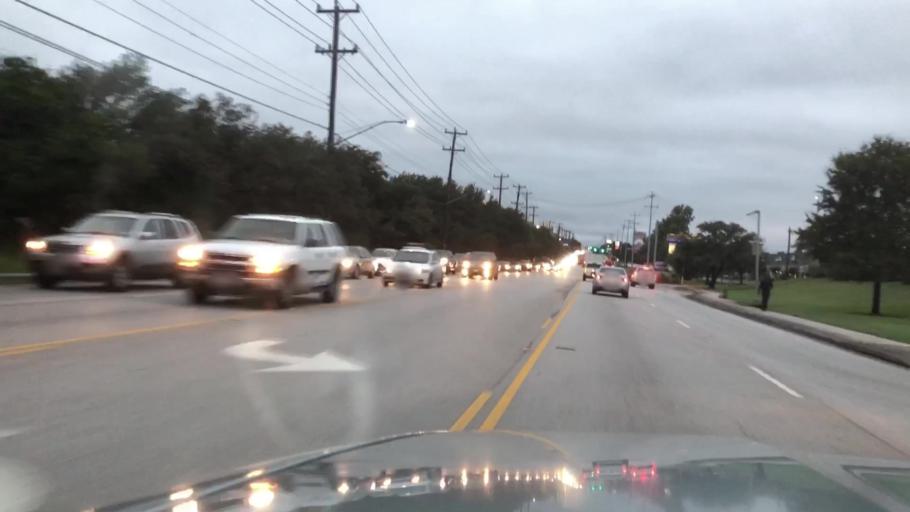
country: US
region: Texas
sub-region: Bexar County
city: Shavano Park
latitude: 29.5631
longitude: -98.5954
